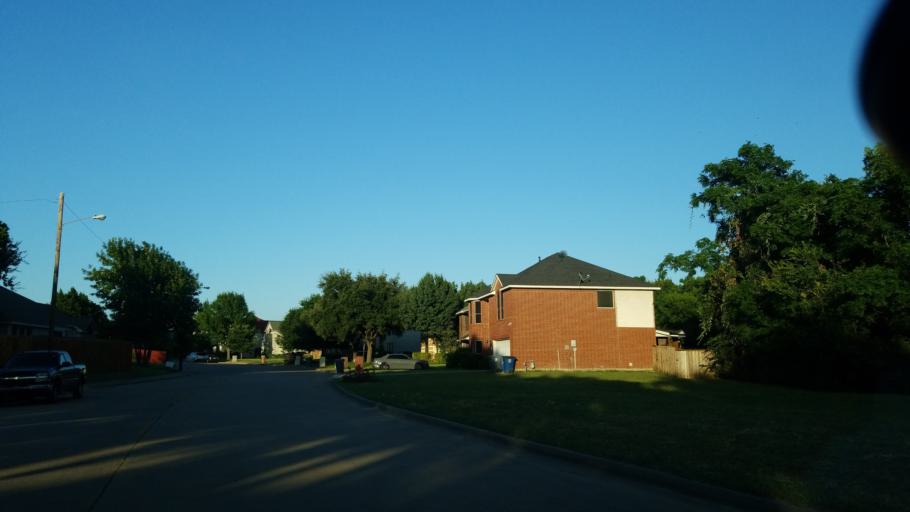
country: US
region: Texas
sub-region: Dallas County
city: Balch Springs
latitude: 32.7858
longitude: -96.6953
